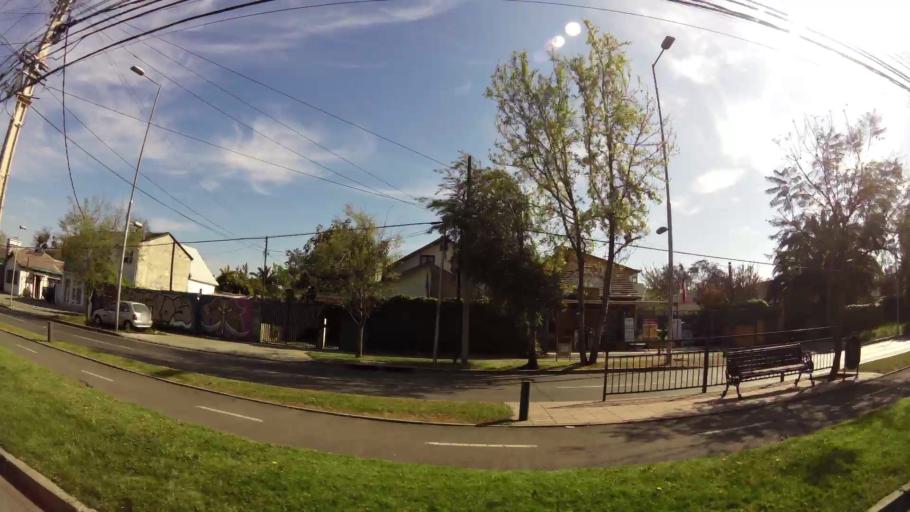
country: CL
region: Santiago Metropolitan
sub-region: Provincia de Santiago
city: Villa Presidente Frei, Nunoa, Santiago, Chile
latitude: -33.4514
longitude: -70.5524
